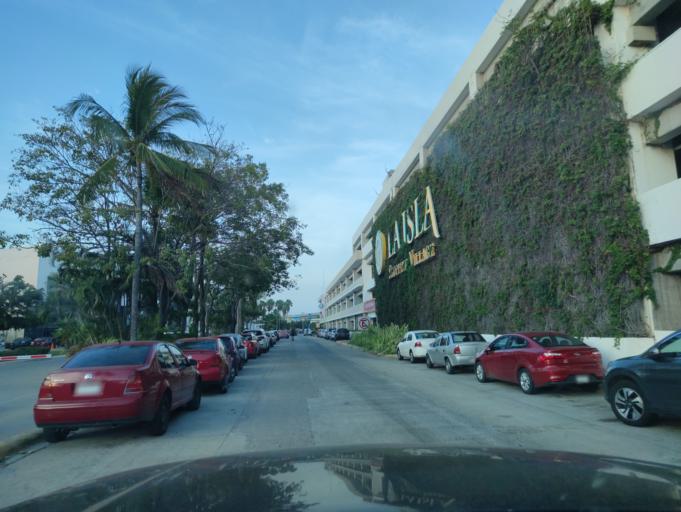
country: MX
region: Guerrero
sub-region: Acapulco de Juarez
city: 10 de Abril
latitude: 16.7707
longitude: -99.7758
